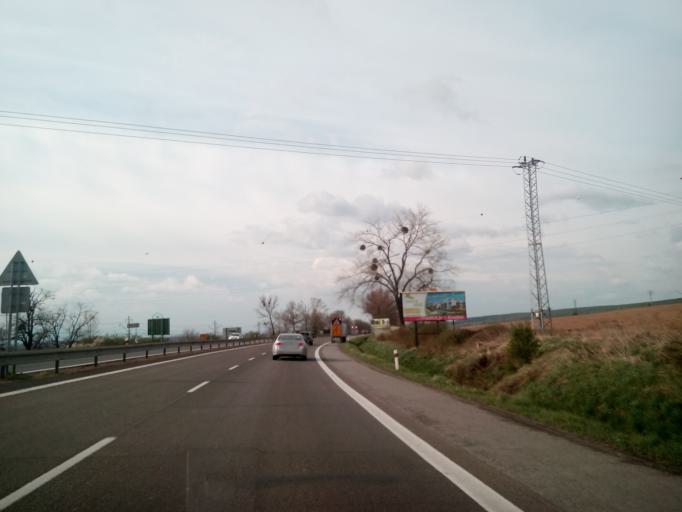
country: SK
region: Kosicky
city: Kosice
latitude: 48.6785
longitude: 21.2138
